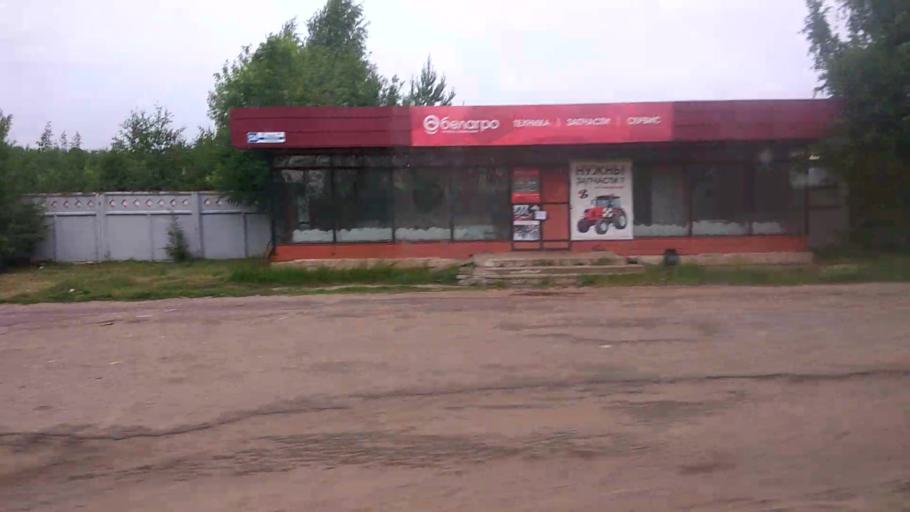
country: RU
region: Moskovskaya
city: Lukhovitsy
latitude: 54.9243
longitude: 38.9954
